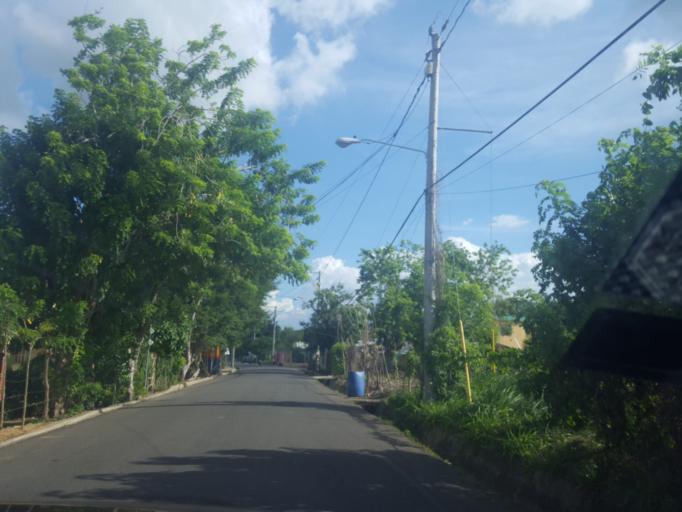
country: DO
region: Santiago
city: Licey al Medio
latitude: 19.3773
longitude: -70.6233
